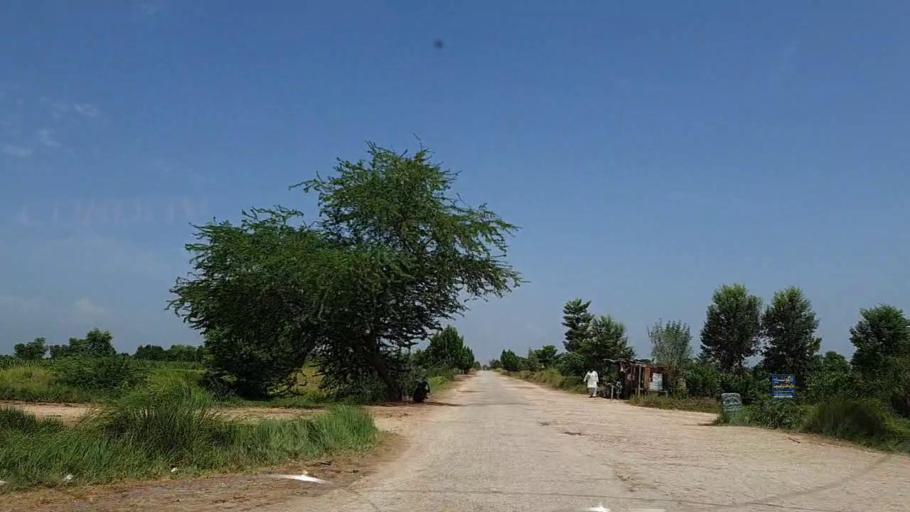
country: PK
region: Sindh
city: Naushahro Firoz
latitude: 26.8216
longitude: 68.1655
